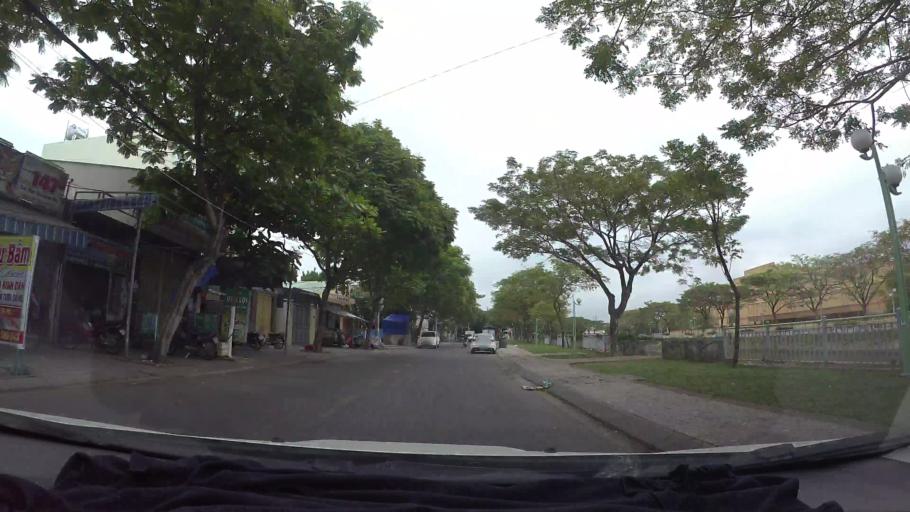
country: VN
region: Da Nang
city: Thanh Khe
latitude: 16.0721
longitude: 108.1817
